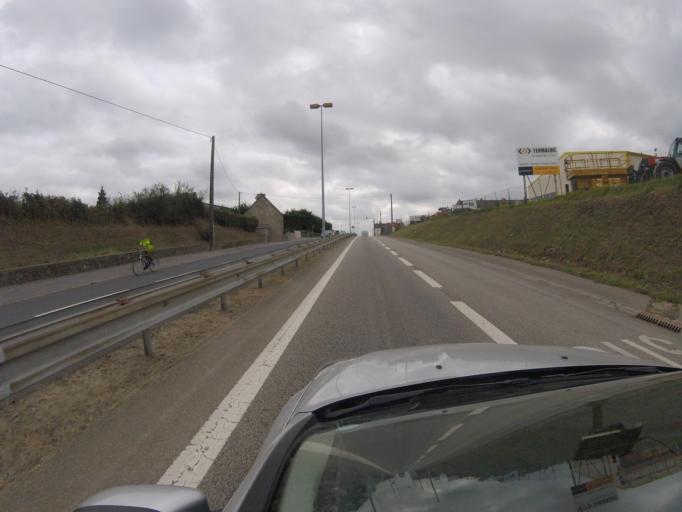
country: FR
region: Lower Normandy
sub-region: Departement de la Manche
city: La Glacerie
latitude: 49.6100
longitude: -1.6004
